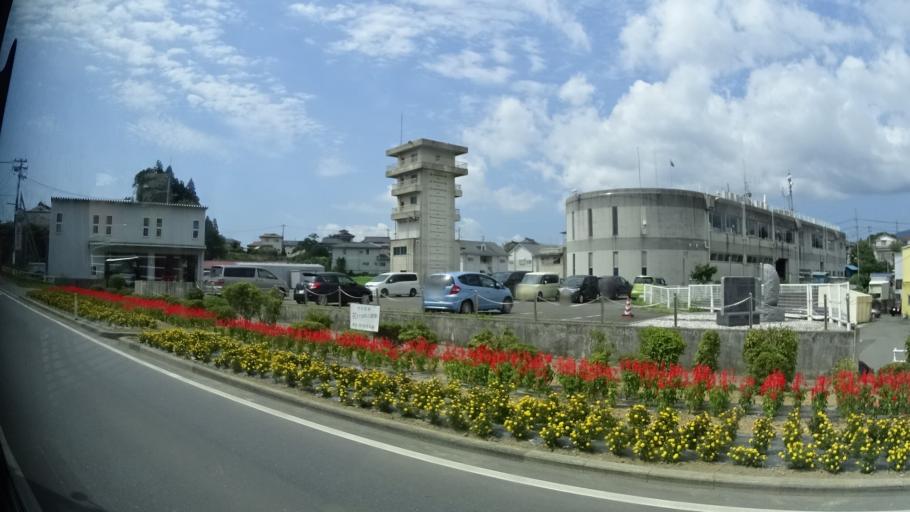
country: JP
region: Iwate
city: Ofunato
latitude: 38.8813
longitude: 141.5754
